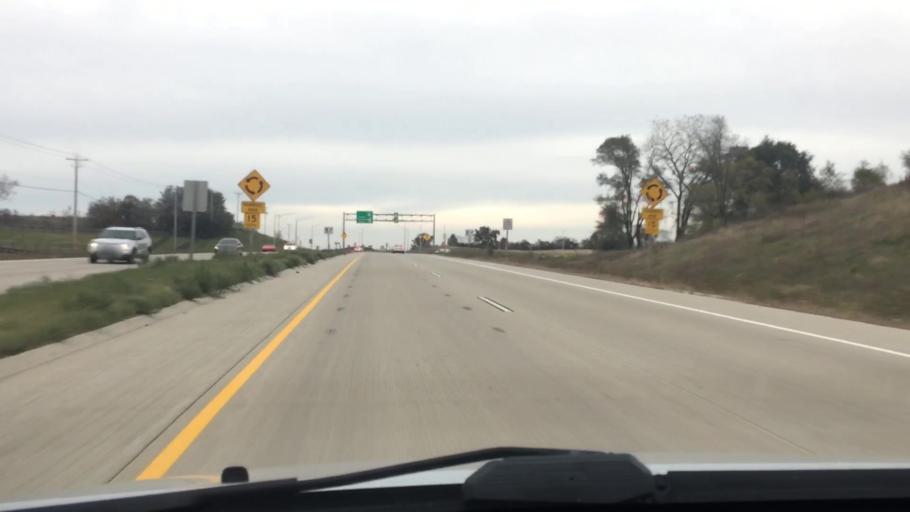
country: US
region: Wisconsin
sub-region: Waukesha County
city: North Prairie
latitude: 42.9318
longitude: -88.3463
